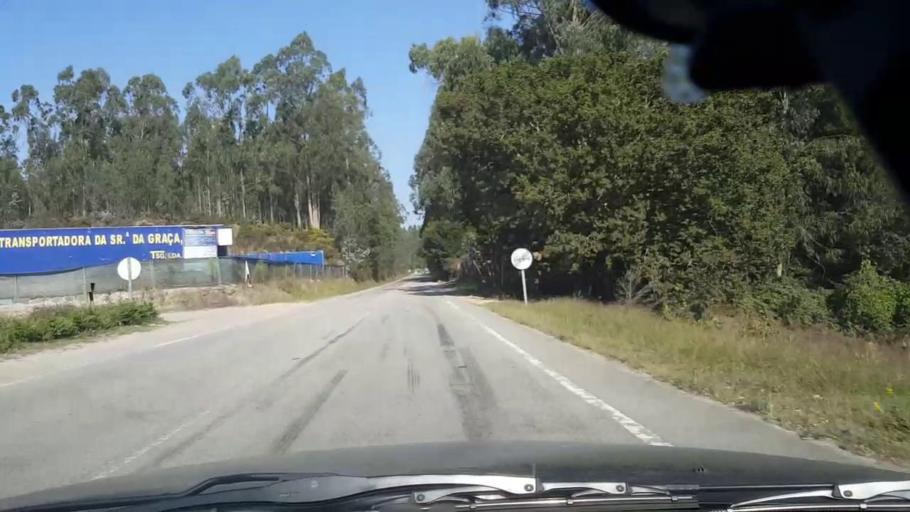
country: PT
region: Porto
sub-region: Vila do Conde
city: Arvore
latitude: 41.3510
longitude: -8.6848
